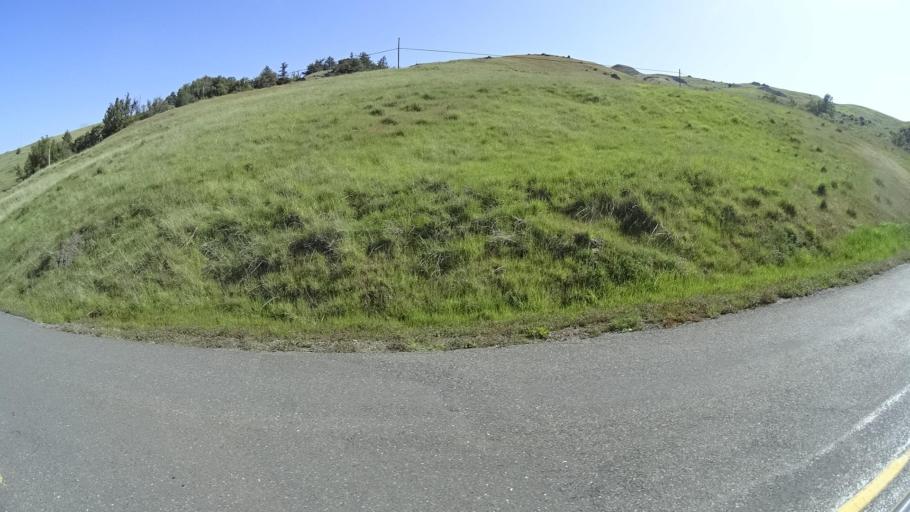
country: US
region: California
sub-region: Humboldt County
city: Redway
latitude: 40.1085
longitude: -123.7159
